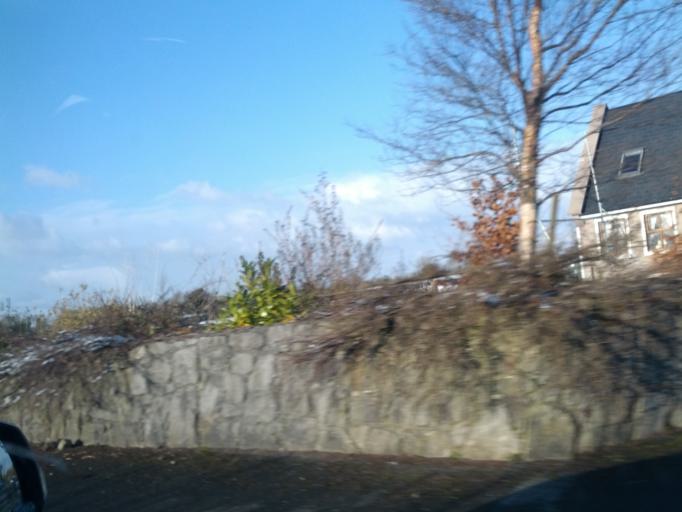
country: IE
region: Connaught
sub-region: County Galway
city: Athenry
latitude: 53.1879
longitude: -8.7262
